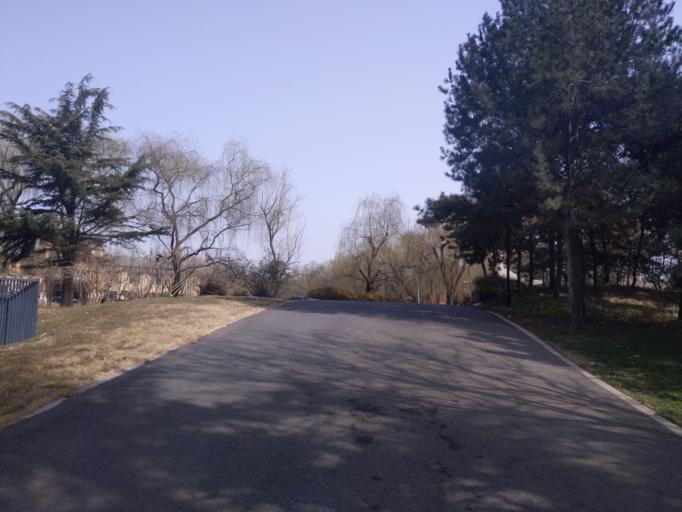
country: CN
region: Henan Sheng
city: Puyang
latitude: 35.7756
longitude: 114.9591
